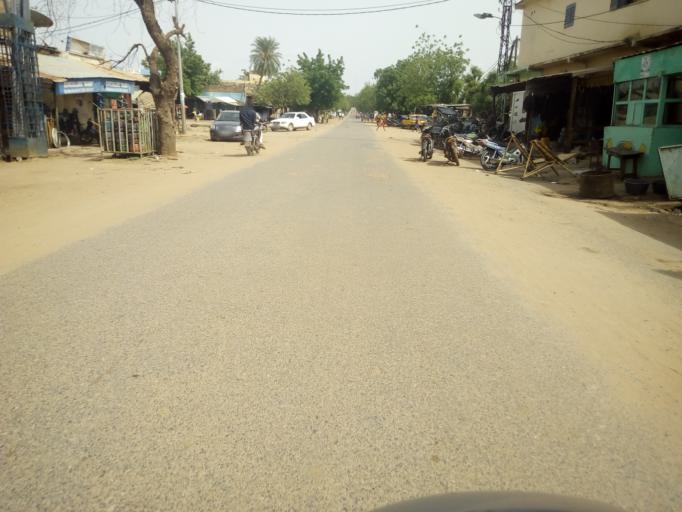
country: ML
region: Kayes
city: Kayes
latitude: 14.4446
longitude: -11.4382
